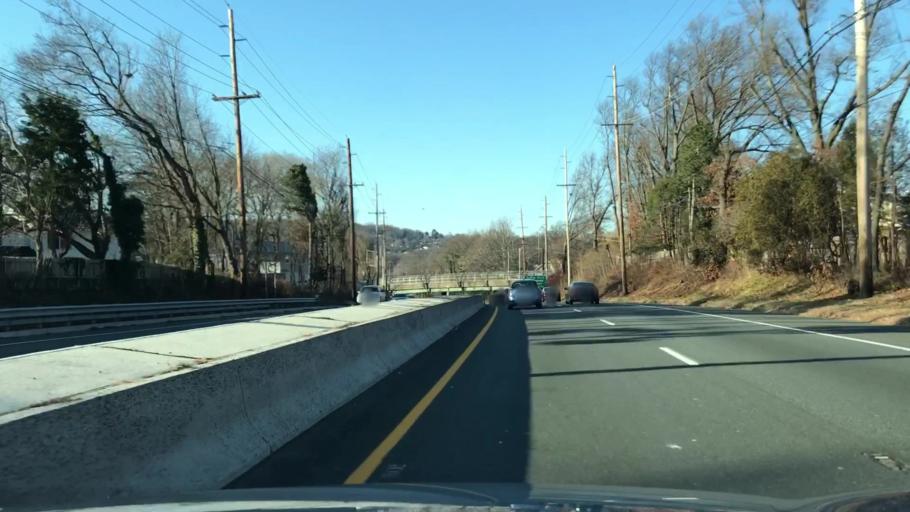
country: US
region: New Jersey
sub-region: Bergen County
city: Glen Rock
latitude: 40.9626
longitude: -74.1470
